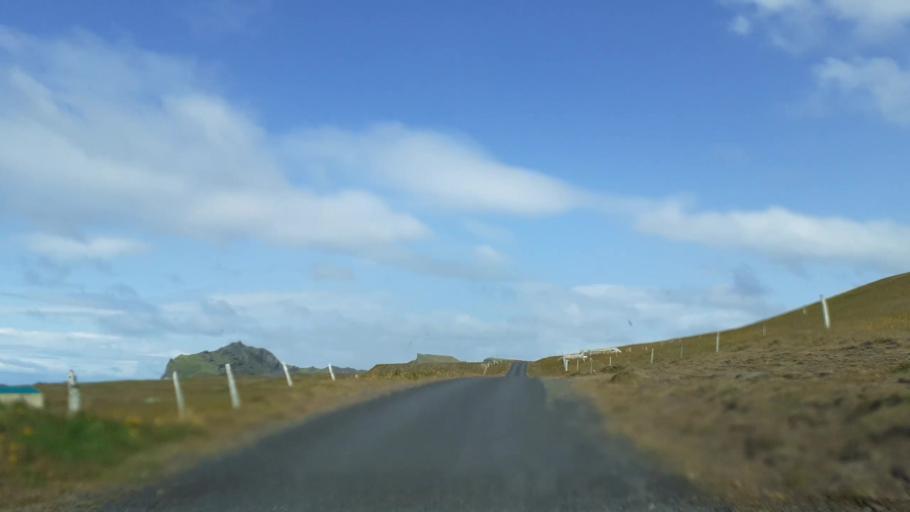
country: IS
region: South
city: Vestmannaeyjar
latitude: 63.4165
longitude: -20.2813
